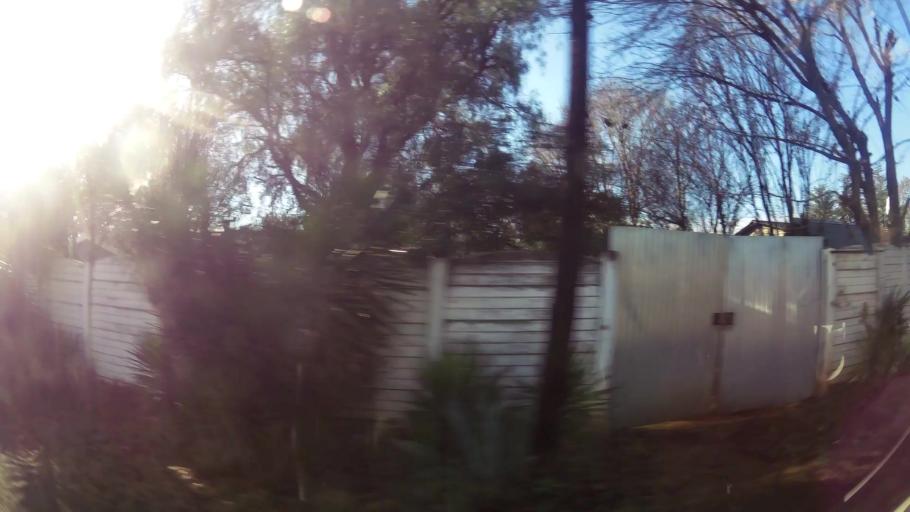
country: ZA
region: Gauteng
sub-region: Sedibeng District Municipality
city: Meyerton
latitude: -26.4969
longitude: 28.0699
